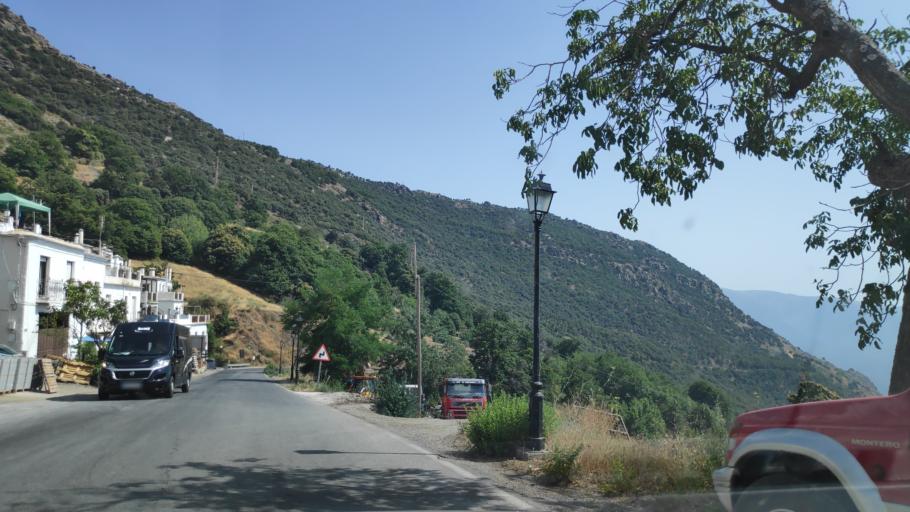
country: ES
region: Andalusia
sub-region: Provincia de Granada
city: Bubion
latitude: 36.9468
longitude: -3.3544
